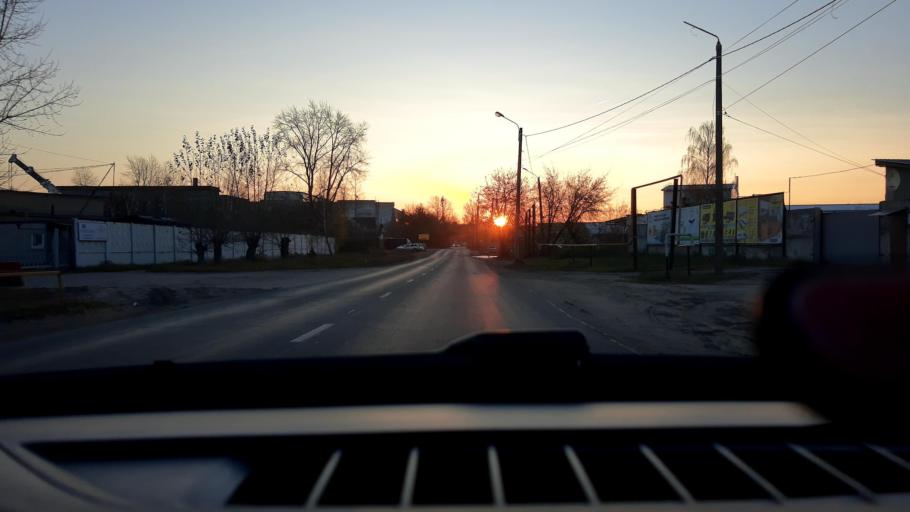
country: RU
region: Nizjnij Novgorod
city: Gorbatovka
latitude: 56.3479
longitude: 43.8168
